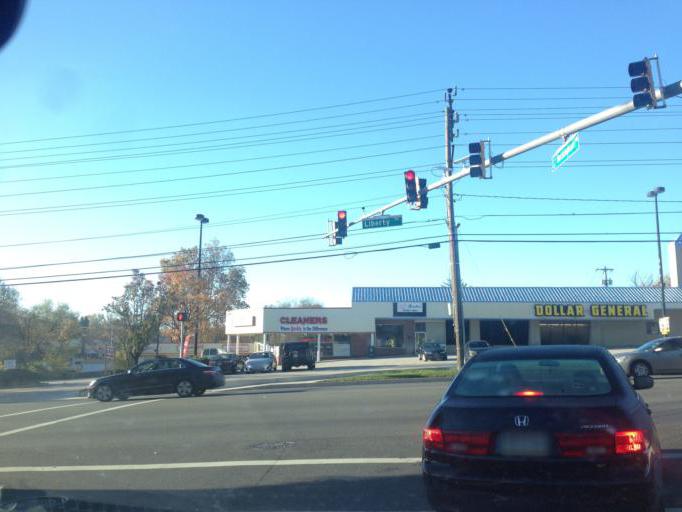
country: US
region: Maryland
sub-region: Baltimore County
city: Lochearn
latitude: 39.3476
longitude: -76.7402
